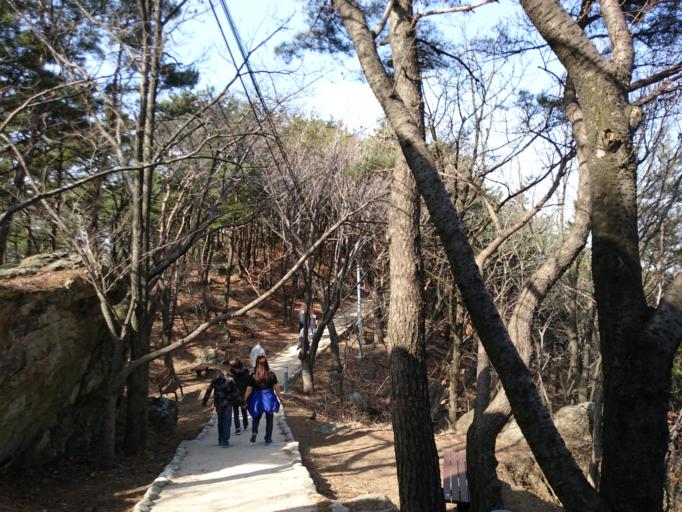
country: KR
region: Daegu
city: Daegu
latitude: 35.8230
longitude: 128.5791
